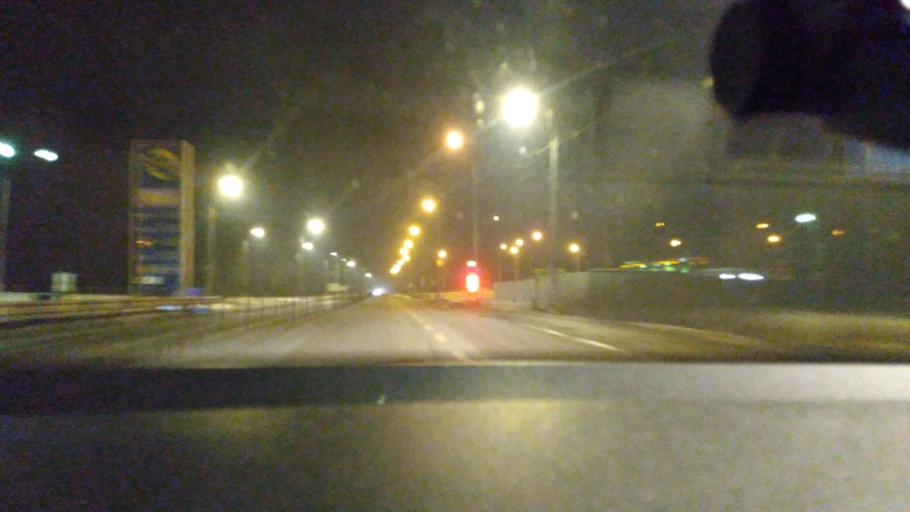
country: RU
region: Moskovskaya
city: Yegor'yevsk
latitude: 55.4167
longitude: 39.0443
